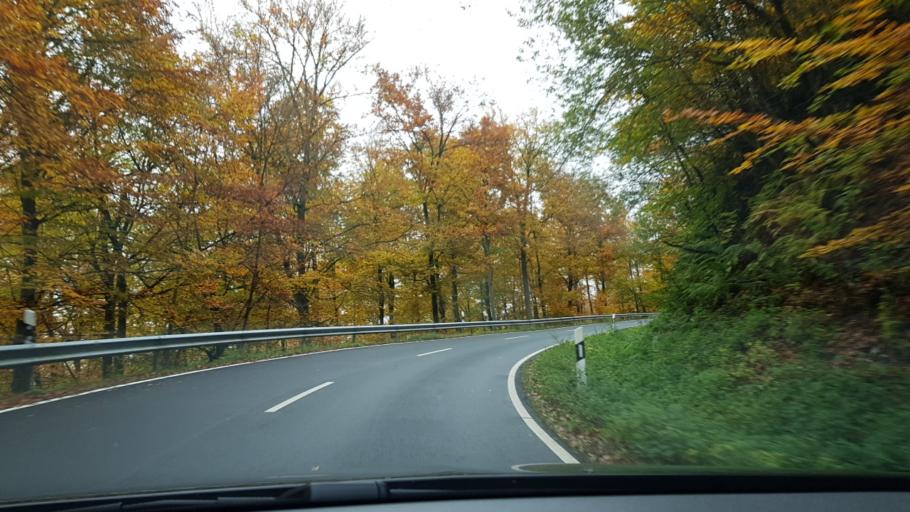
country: DE
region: Rheinland-Pfalz
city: Polich
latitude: 49.7818
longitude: 6.8436
